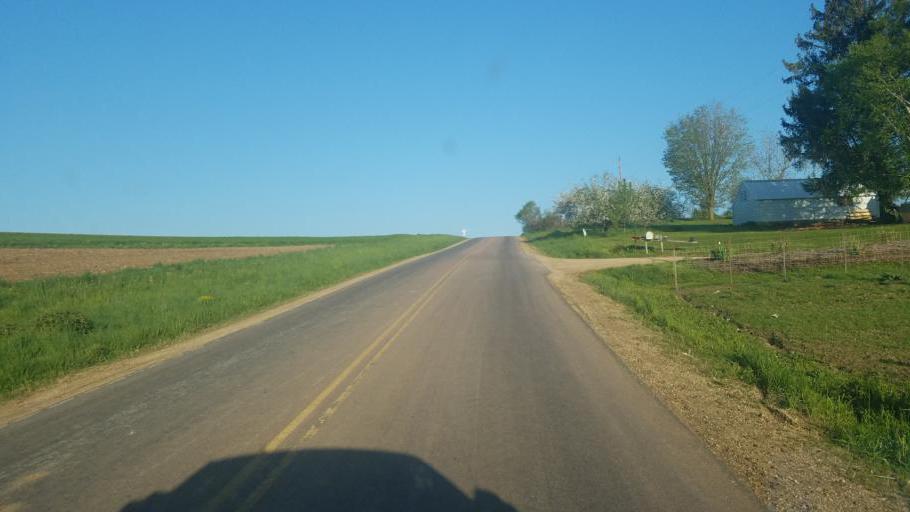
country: US
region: Wisconsin
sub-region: Vernon County
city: Hillsboro
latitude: 43.6462
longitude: -90.4455
